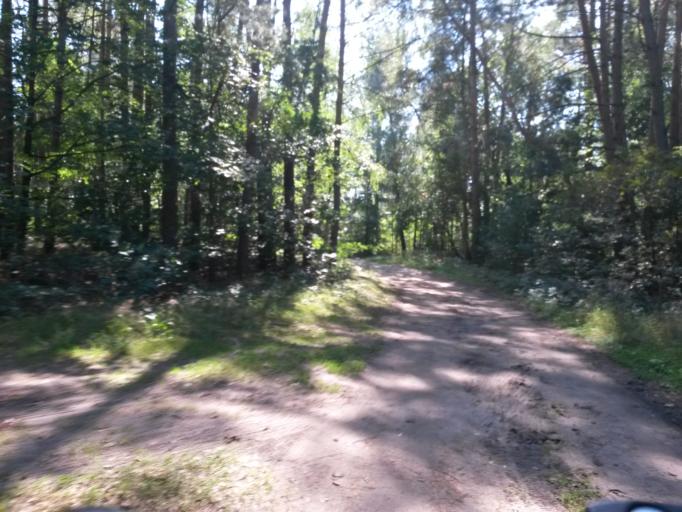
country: DE
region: Brandenburg
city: Zehdenick
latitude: 53.0413
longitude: 13.4088
